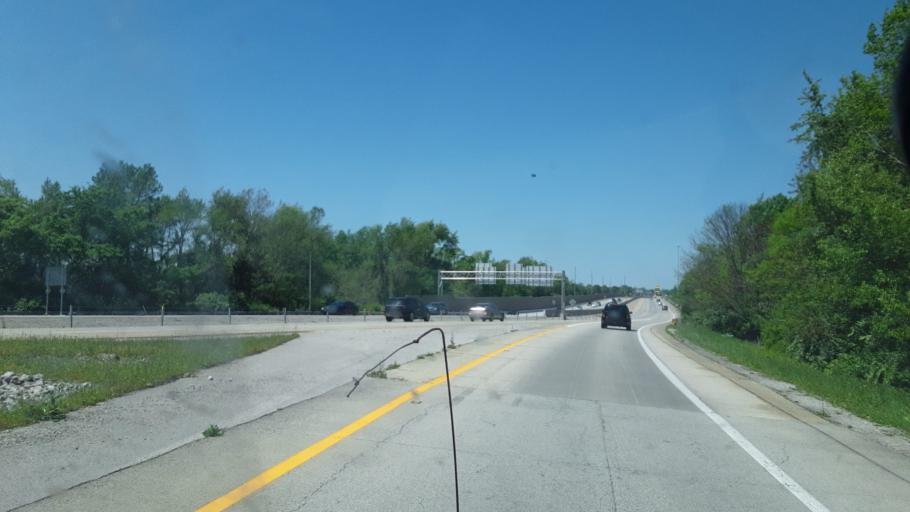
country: US
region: Kentucky
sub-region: Jefferson County
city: Worthington
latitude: 38.3168
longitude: -85.5863
